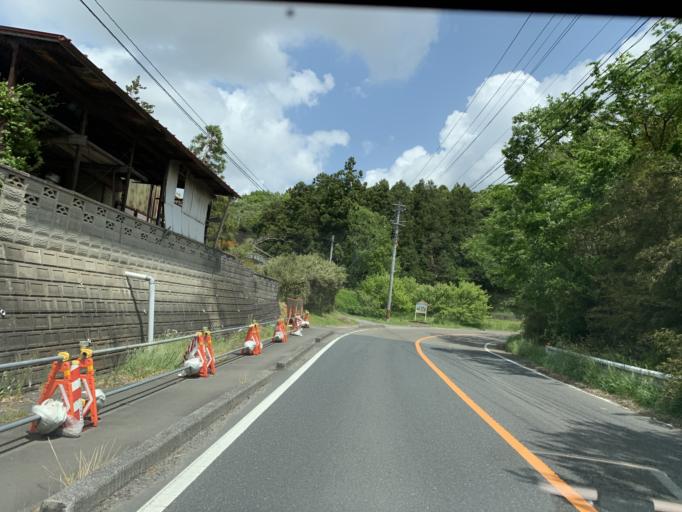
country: JP
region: Miyagi
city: Kogota
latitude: 38.6545
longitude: 141.0579
